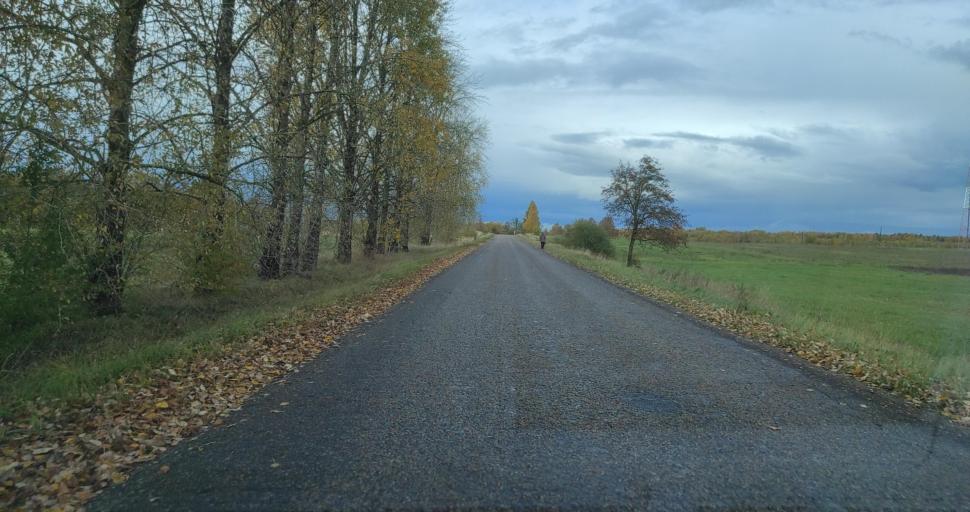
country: LV
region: Vainode
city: Vainode
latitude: 56.5737
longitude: 21.8926
